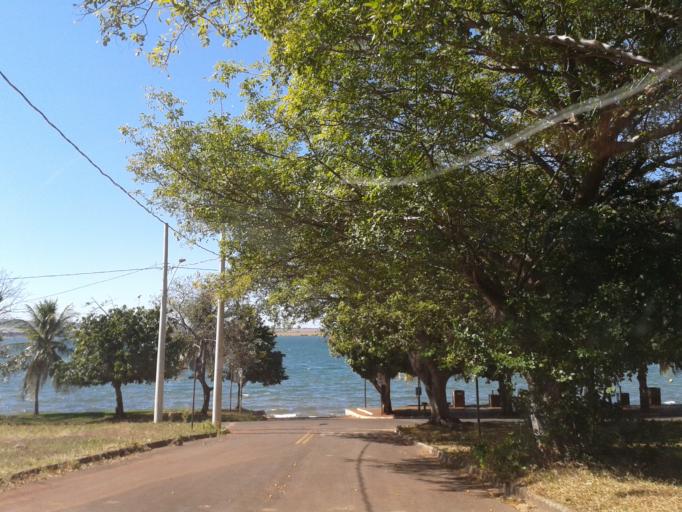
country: BR
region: Minas Gerais
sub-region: Capinopolis
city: Capinopolis
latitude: -18.5172
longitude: -49.4980
